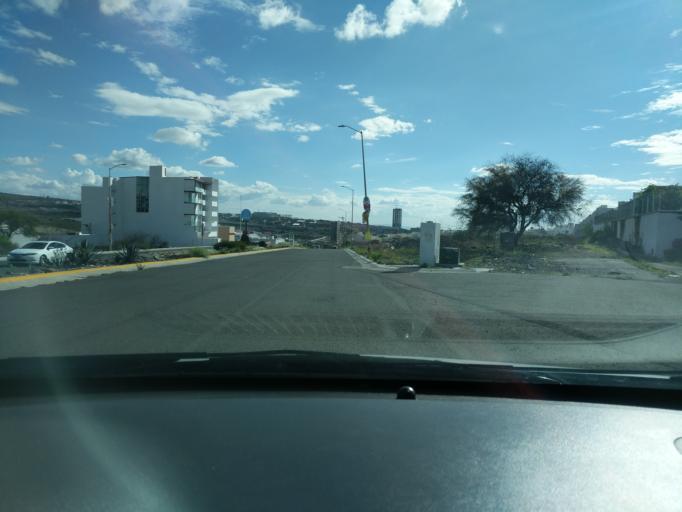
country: MX
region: Queretaro
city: La Canada
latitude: 20.5922
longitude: -100.3278
